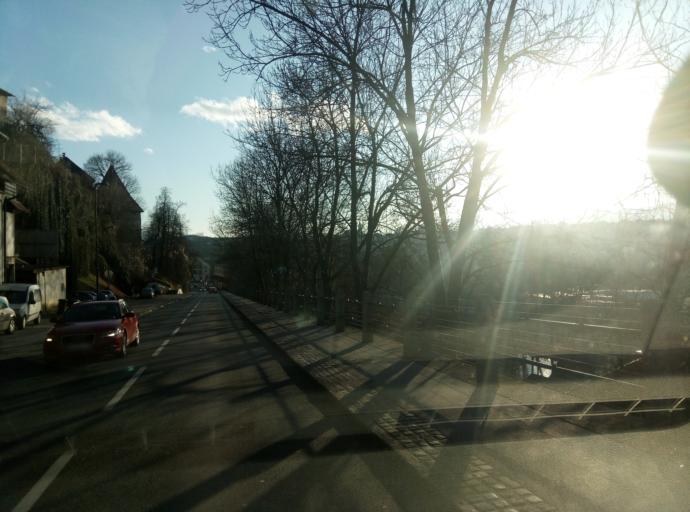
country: SI
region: Kranj
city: Kranj
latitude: 46.2408
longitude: 14.3545
